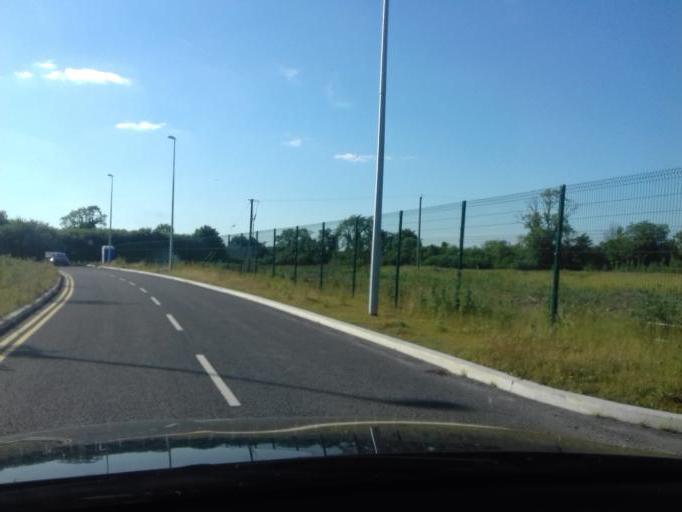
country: IE
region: Leinster
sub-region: Fingal County
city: Blanchardstown
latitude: 53.4241
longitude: -6.3819
